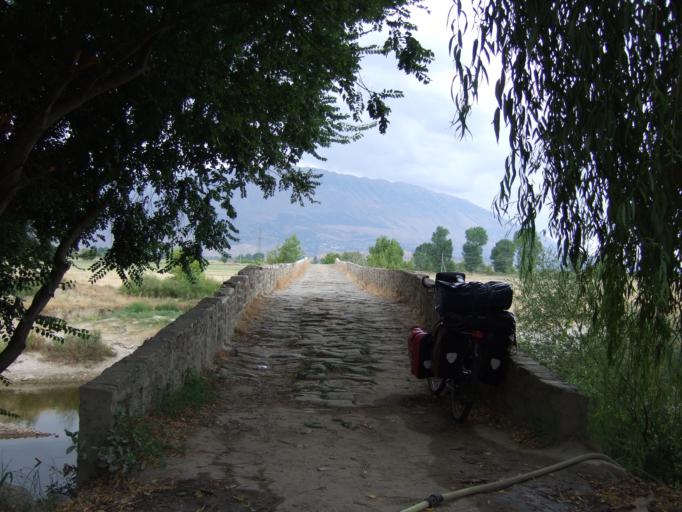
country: AL
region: Gjirokaster
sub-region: Rrethi i Gjirokastres
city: Dervician
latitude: 40.0612
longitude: 20.1731
